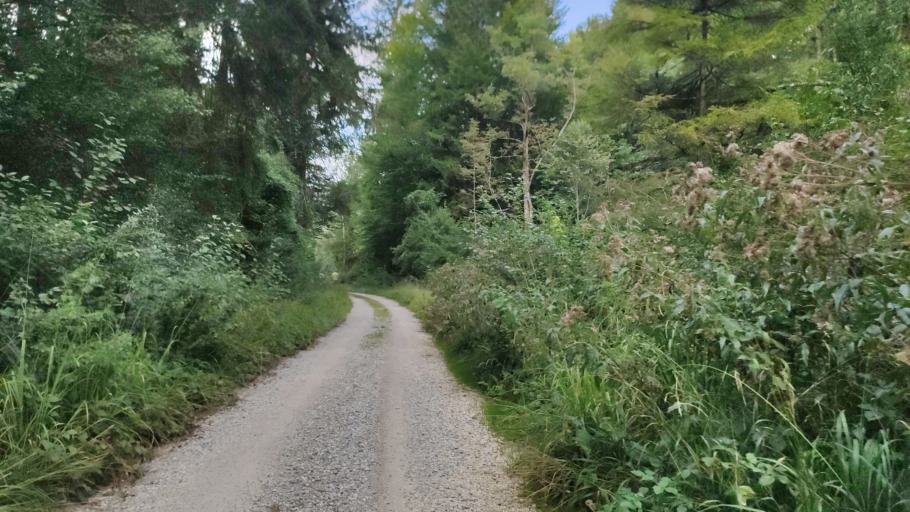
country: DE
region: Bavaria
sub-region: Upper Bavaria
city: Kaufering
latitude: 48.1296
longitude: 10.8613
